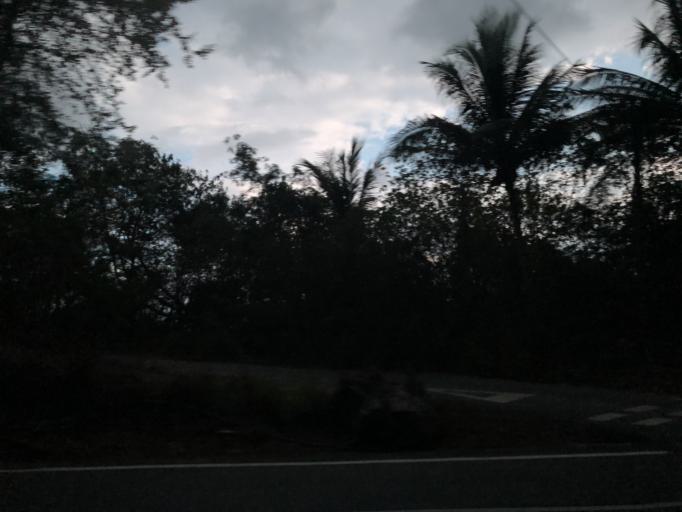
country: TW
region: Taiwan
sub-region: Taitung
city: Taitung
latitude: 22.8616
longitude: 121.2025
